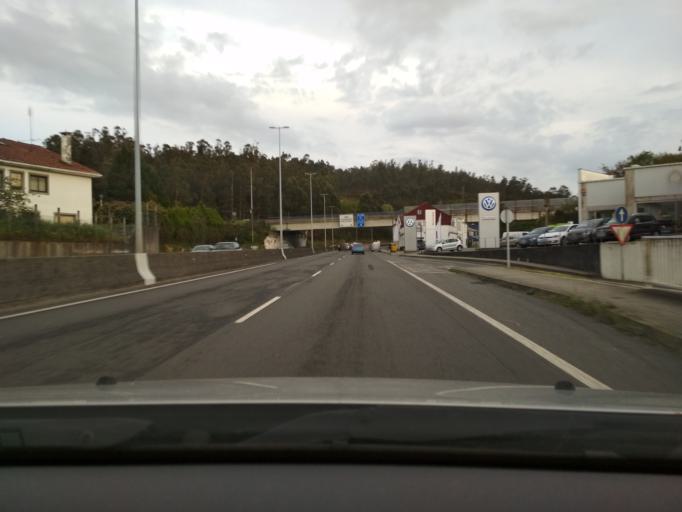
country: ES
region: Galicia
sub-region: Provincia da Coruna
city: Santiago de Compostela
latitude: 42.8577
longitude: -8.5717
